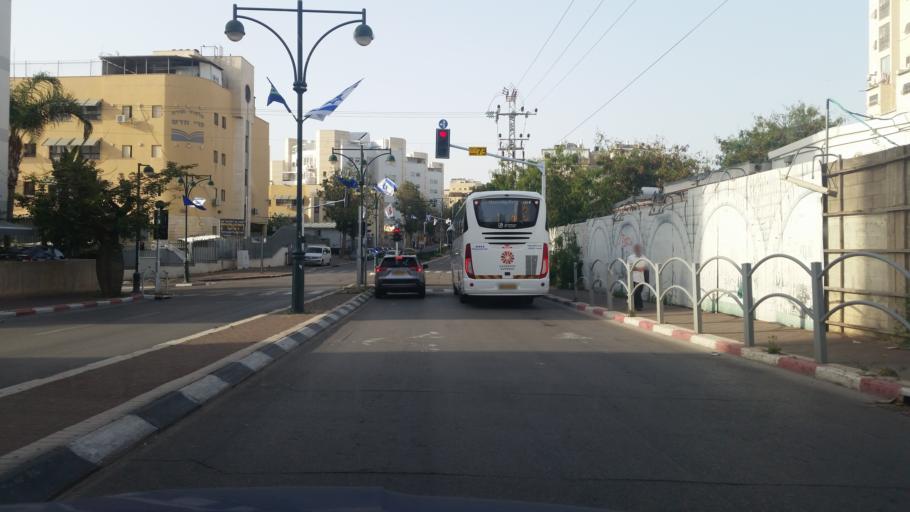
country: IL
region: Tel Aviv
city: Bene Beraq
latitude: 32.0746
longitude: 34.8331
